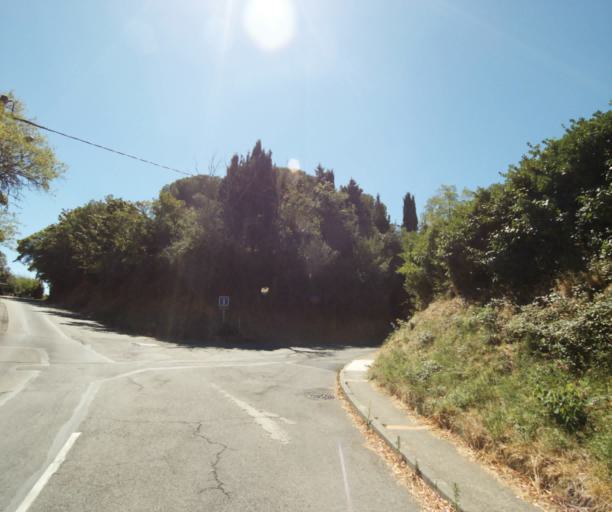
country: FR
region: Midi-Pyrenees
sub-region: Departement de la Haute-Garonne
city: Castanet-Tolosan
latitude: 43.5129
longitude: 1.4944
